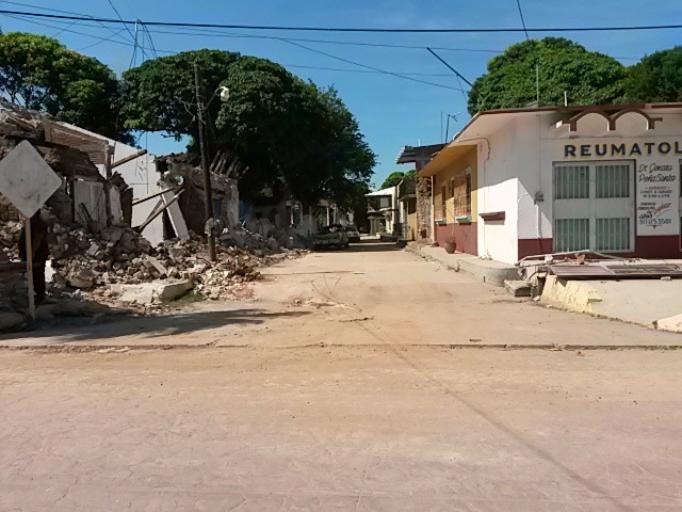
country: MX
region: Oaxaca
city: Asuncion Ixtaltepec
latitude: 16.5040
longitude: -95.0567
